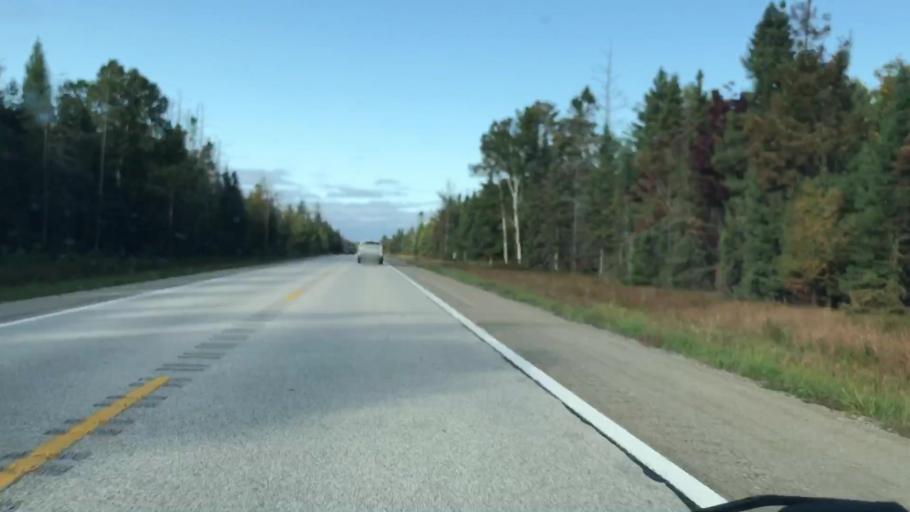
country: US
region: Michigan
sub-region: Luce County
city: Newberry
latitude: 46.3239
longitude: -85.1743
